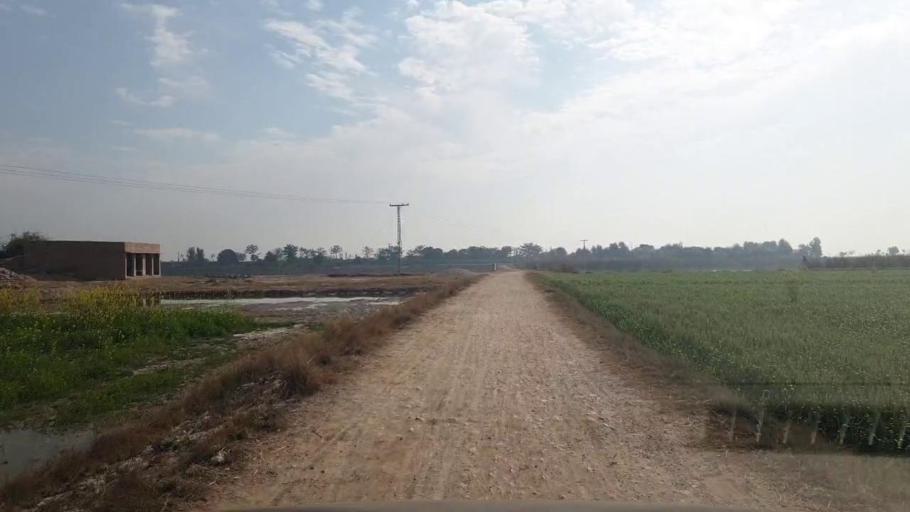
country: PK
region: Sindh
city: Hala
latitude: 25.9916
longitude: 68.4371
